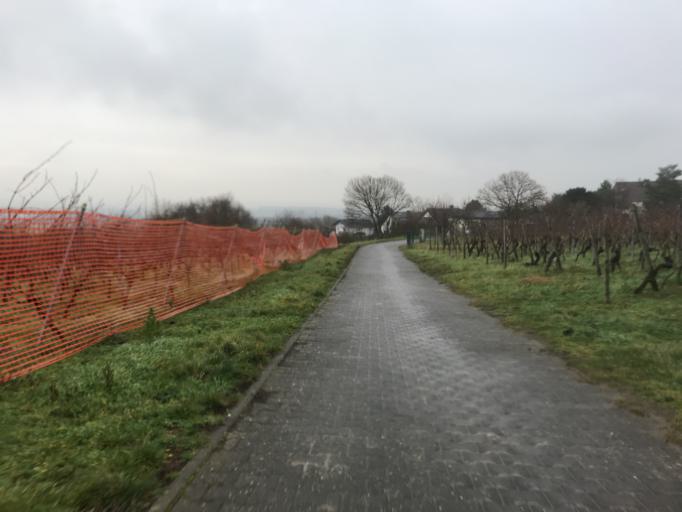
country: DE
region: Rheinland-Pfalz
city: Wackernheim
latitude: 49.9910
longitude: 8.1012
